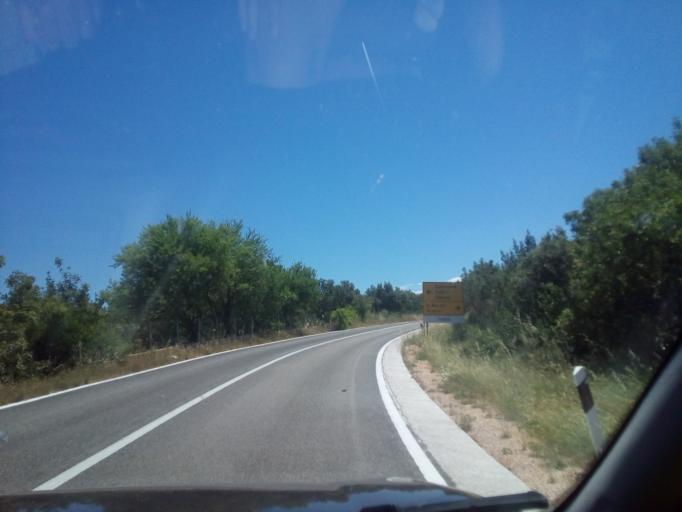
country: HR
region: Sibensko-Kniniska
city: Zaton
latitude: 43.7619
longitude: 15.8372
